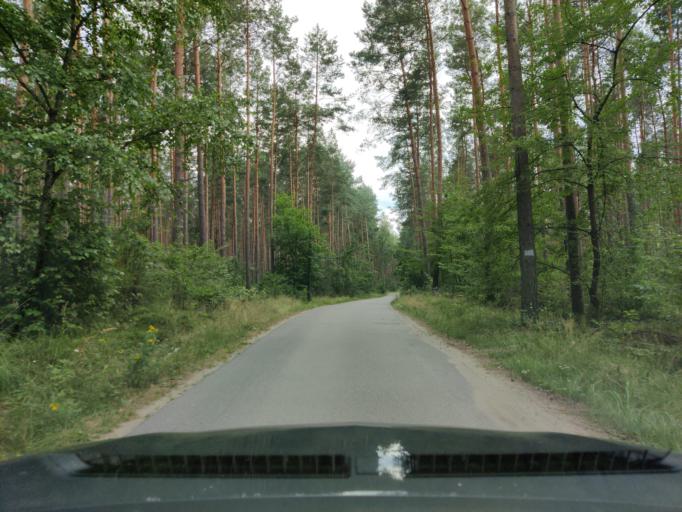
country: PL
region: Masovian Voivodeship
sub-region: Powiat pultuski
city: Pultusk
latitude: 52.7471
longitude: 21.1420
